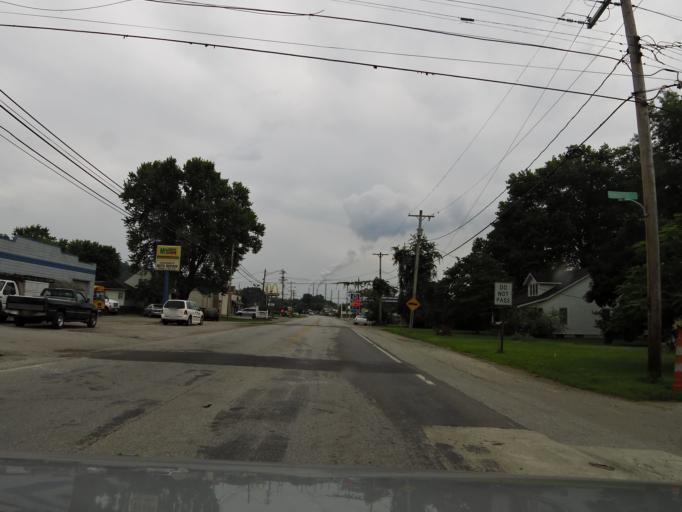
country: US
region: Ohio
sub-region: Brown County
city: Ripley
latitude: 38.7332
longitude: -83.8379
